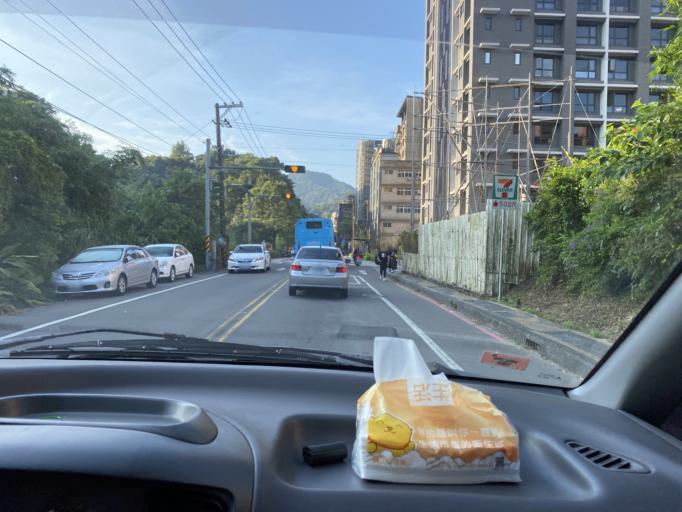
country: TW
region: Taiwan
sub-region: Keelung
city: Keelung
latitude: 25.0969
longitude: 121.7388
